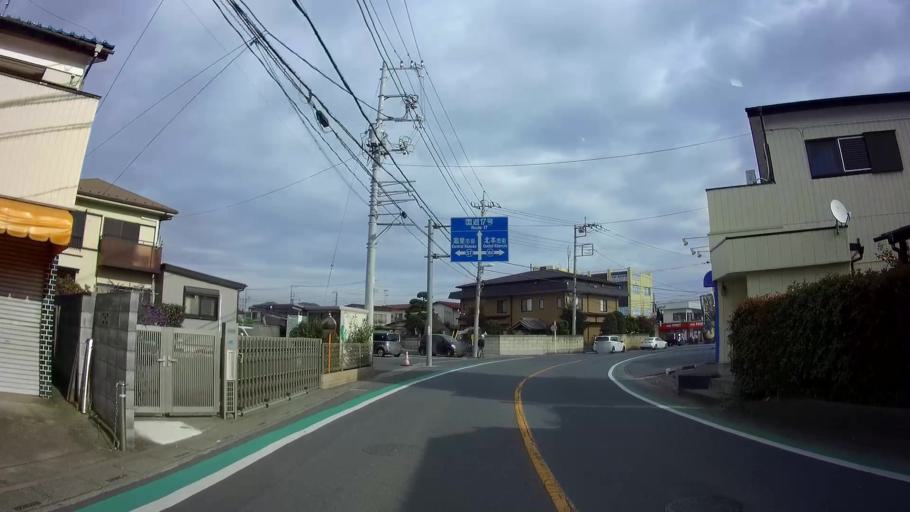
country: JP
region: Saitama
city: Konosu
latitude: 36.0476
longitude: 139.5213
